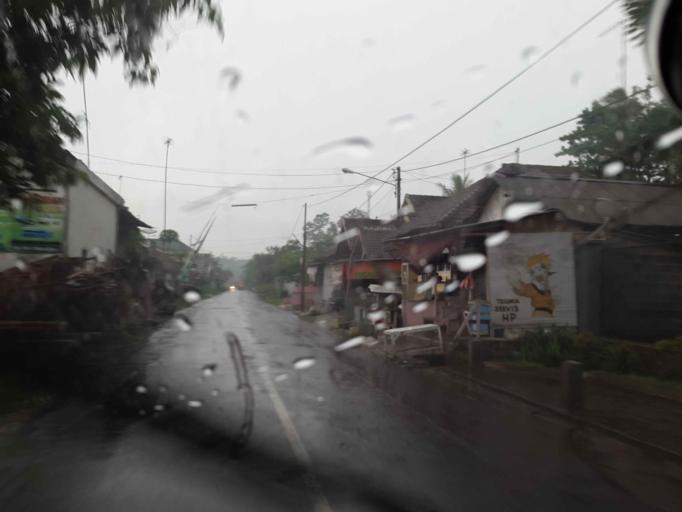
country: ID
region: East Java
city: Kedungkrajan
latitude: -8.1435
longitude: 112.5838
